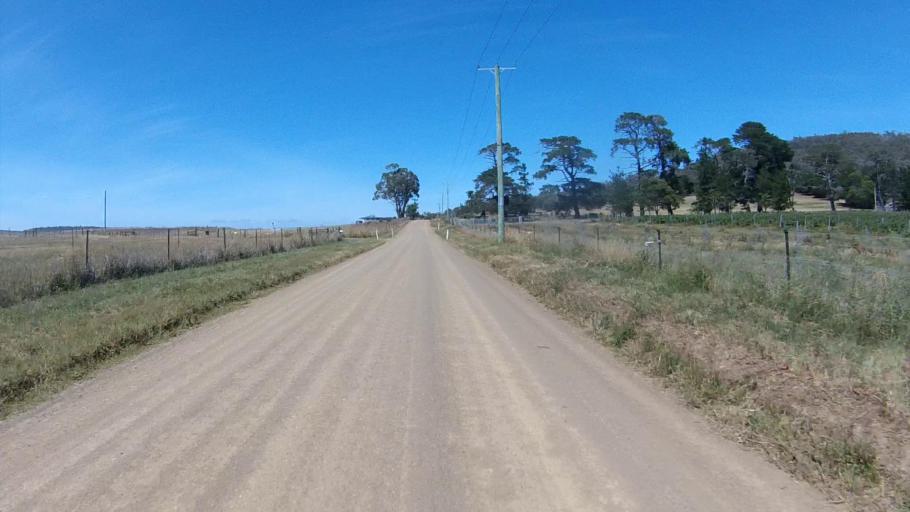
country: AU
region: Tasmania
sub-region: Sorell
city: Sorell
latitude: -42.7864
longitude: 147.6386
